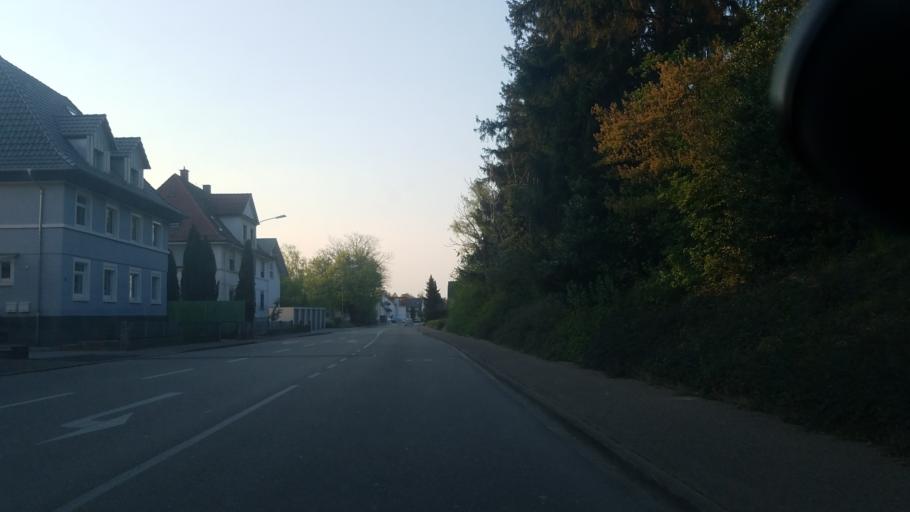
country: DE
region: Baden-Wuerttemberg
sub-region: Freiburg Region
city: Achern
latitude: 48.6326
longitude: 8.0743
